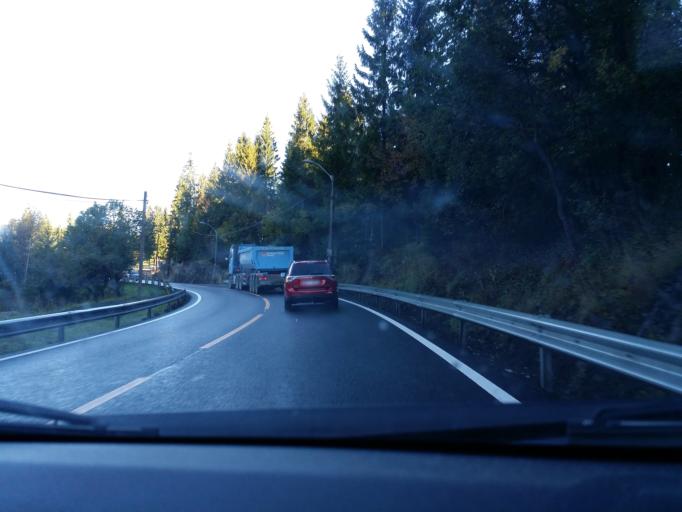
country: NO
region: Akershus
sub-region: Baerum
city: Skui
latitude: 59.9526
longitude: 10.3777
